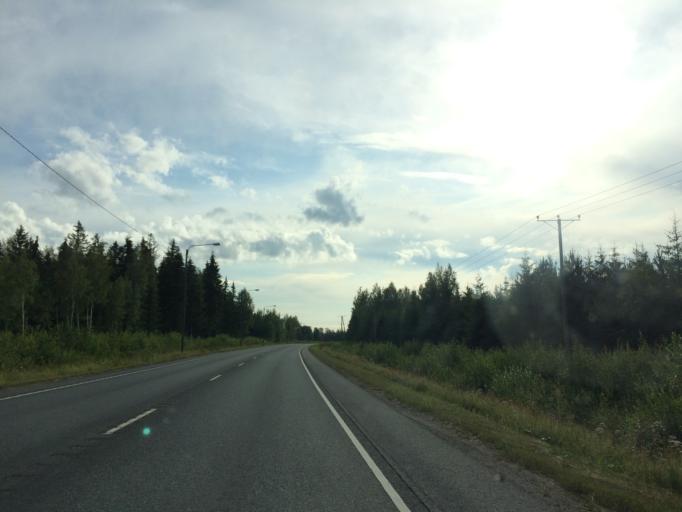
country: FI
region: Haeme
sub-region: Haemeenlinna
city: Janakkala
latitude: 60.9207
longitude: 24.5800
